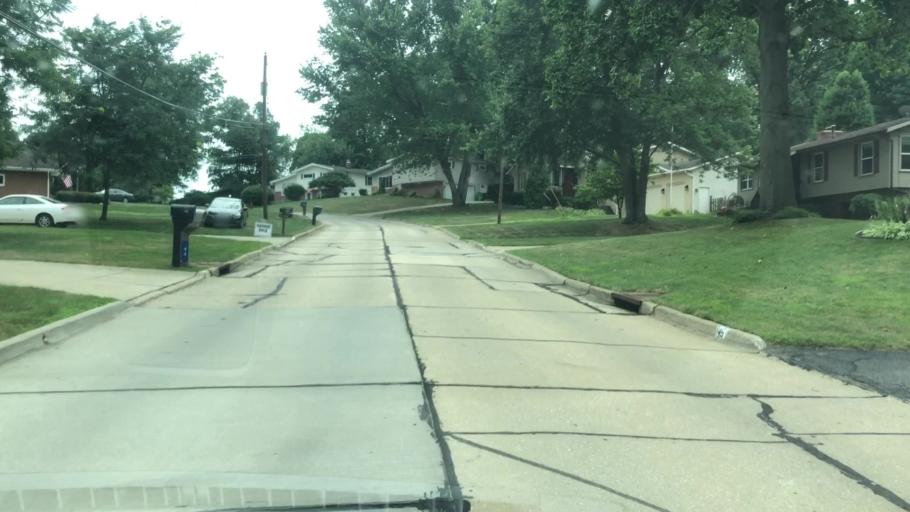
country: US
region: Ohio
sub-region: Summit County
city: Munroe Falls
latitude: 41.1388
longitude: -81.4470
